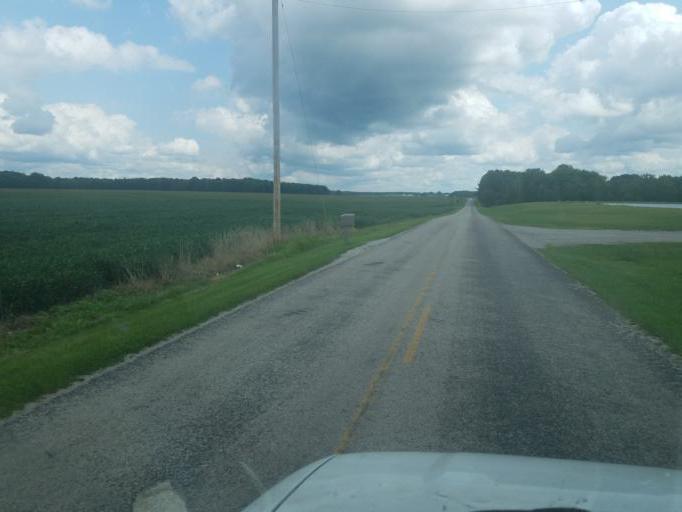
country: US
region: Ohio
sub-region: Ashtabula County
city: Roaming Shores
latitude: 41.5888
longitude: -80.7462
